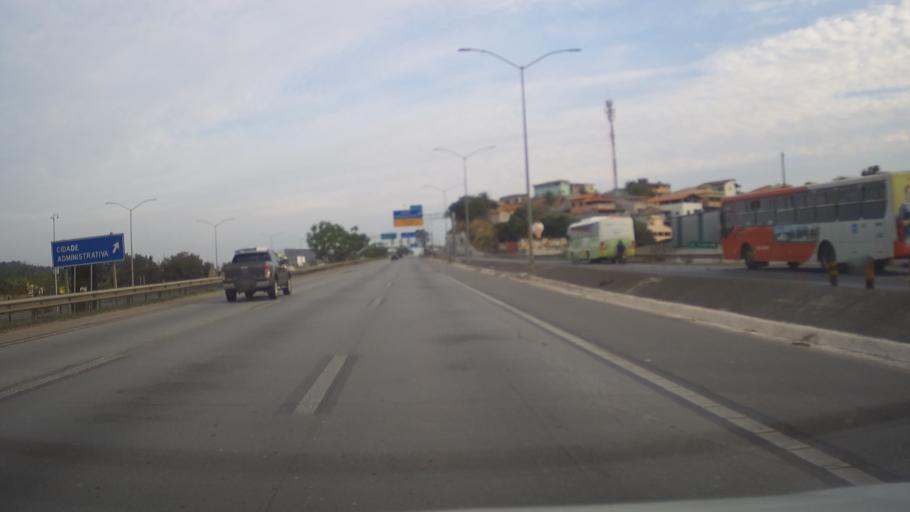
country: BR
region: Minas Gerais
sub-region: Santa Luzia
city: Santa Luzia
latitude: -19.7988
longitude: -43.9500
